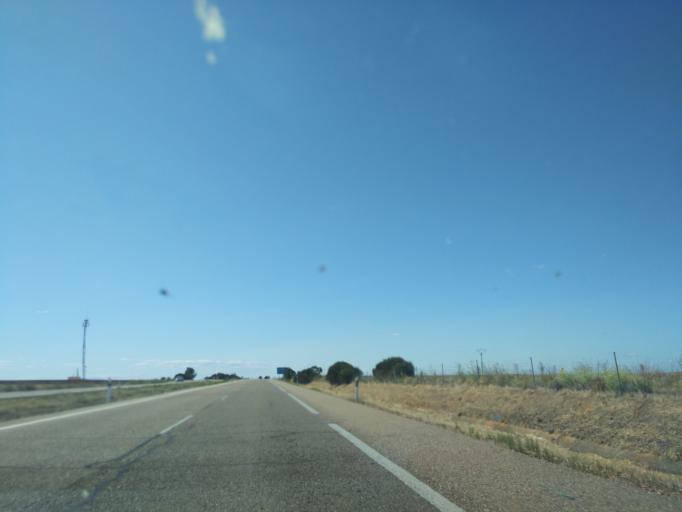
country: ES
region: Castille and Leon
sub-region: Provincia de Zamora
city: Cerecinos de Campos
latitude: 41.8886
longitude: -5.4650
